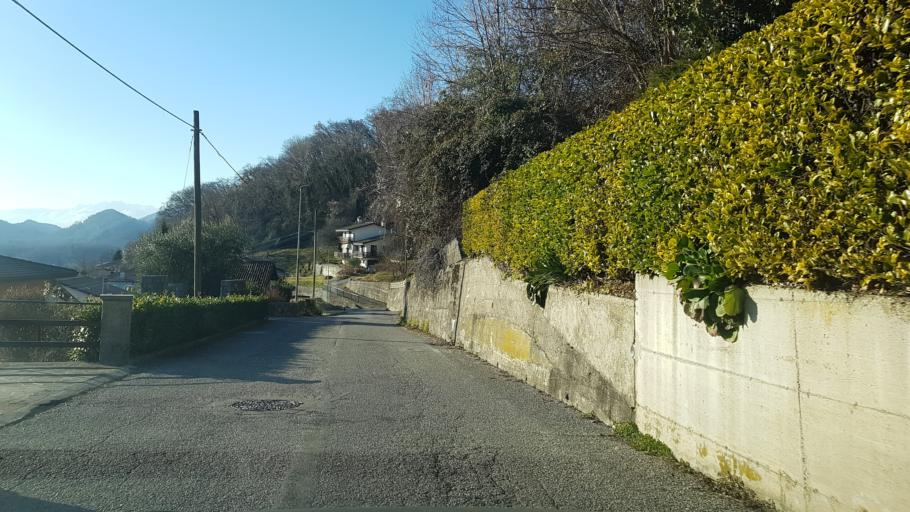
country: IT
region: Friuli Venezia Giulia
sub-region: Provincia di Udine
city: Forgaria nel Friuli
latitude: 46.2256
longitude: 12.9733
